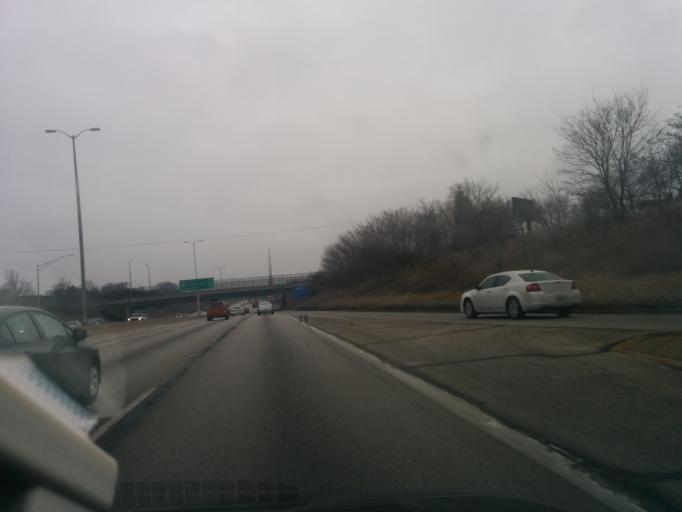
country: US
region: Wisconsin
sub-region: Milwaukee County
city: Milwaukee
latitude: 43.0693
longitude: -87.9209
